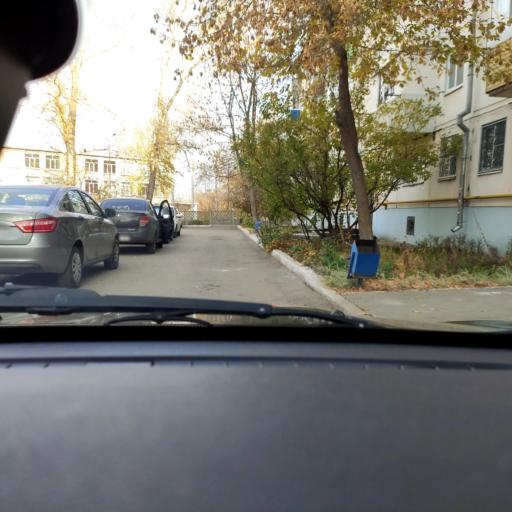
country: RU
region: Samara
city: Tol'yatti
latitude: 53.5079
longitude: 49.4016
